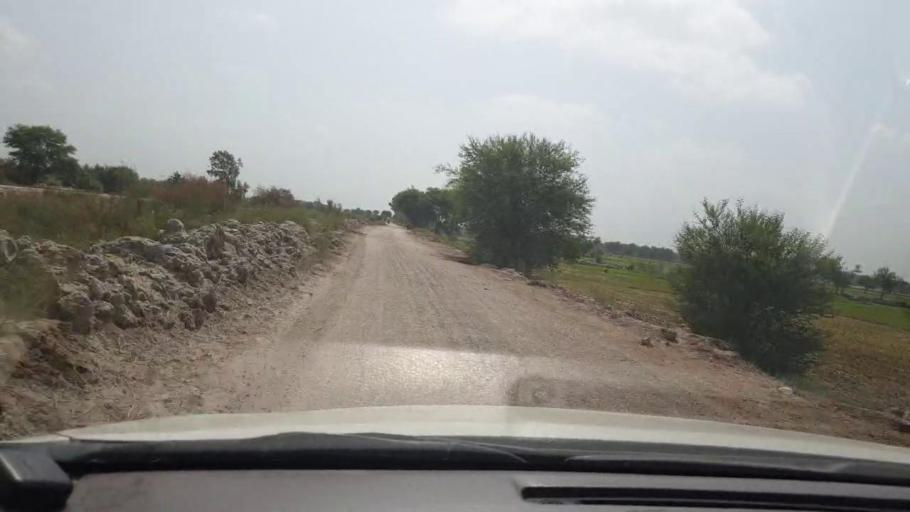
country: PK
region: Sindh
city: Shikarpur
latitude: 28.0096
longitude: 68.5678
